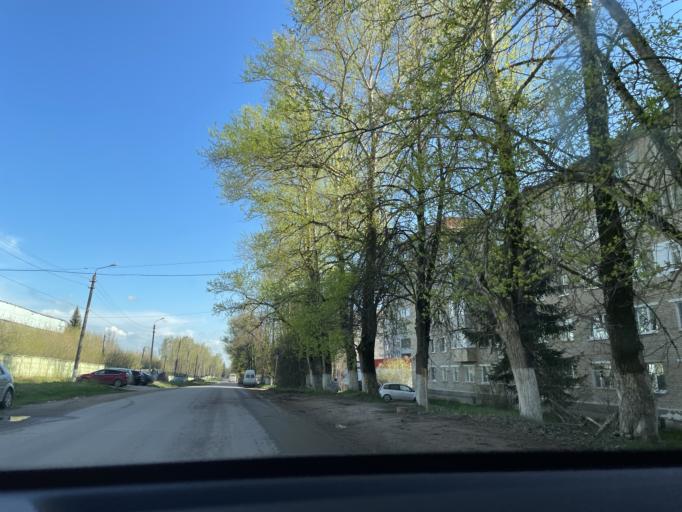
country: RU
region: Tula
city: Aleksin
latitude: 54.4917
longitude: 36.9851
